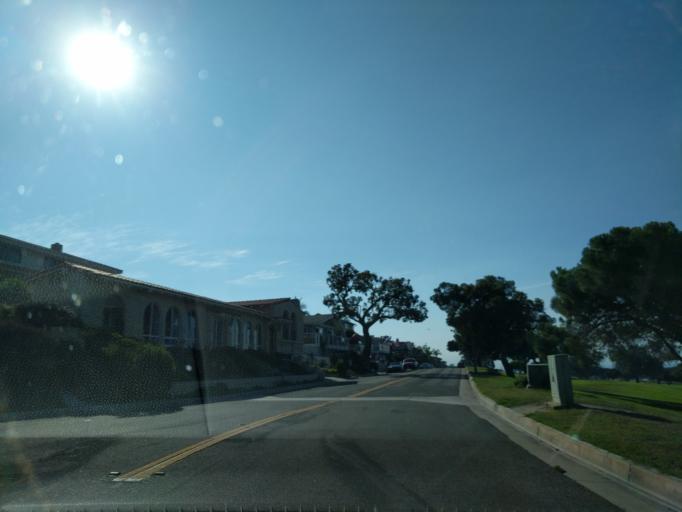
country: US
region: California
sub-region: Orange County
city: San Clemente
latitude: 33.4085
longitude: -117.5933
